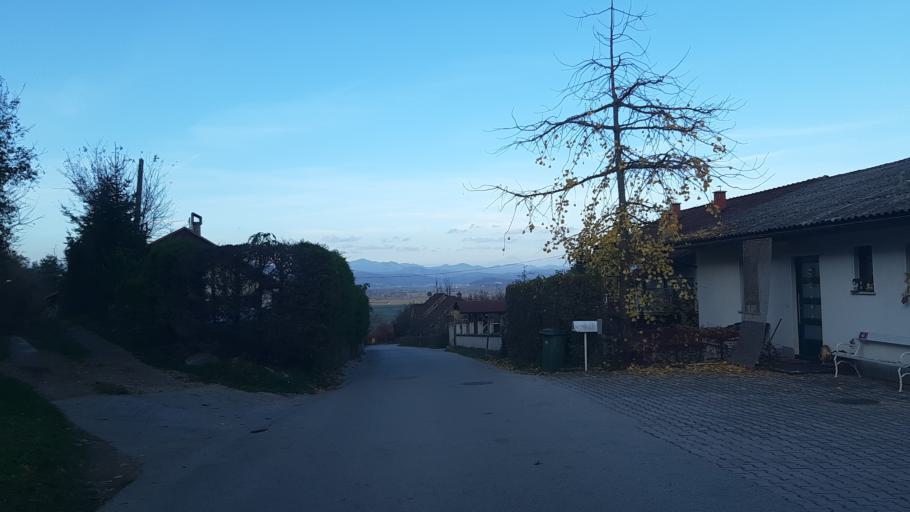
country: SI
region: Borovnica
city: Borovnica
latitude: 45.9239
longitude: 14.3531
